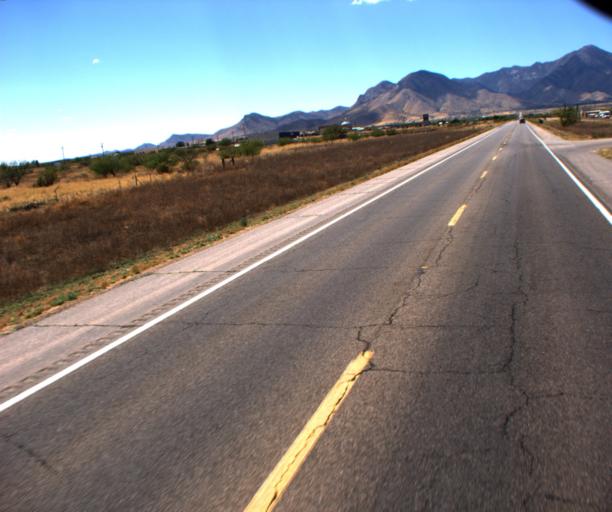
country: US
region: Arizona
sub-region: Cochise County
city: Sierra Vista Southeast
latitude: 31.3799
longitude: -110.1456
